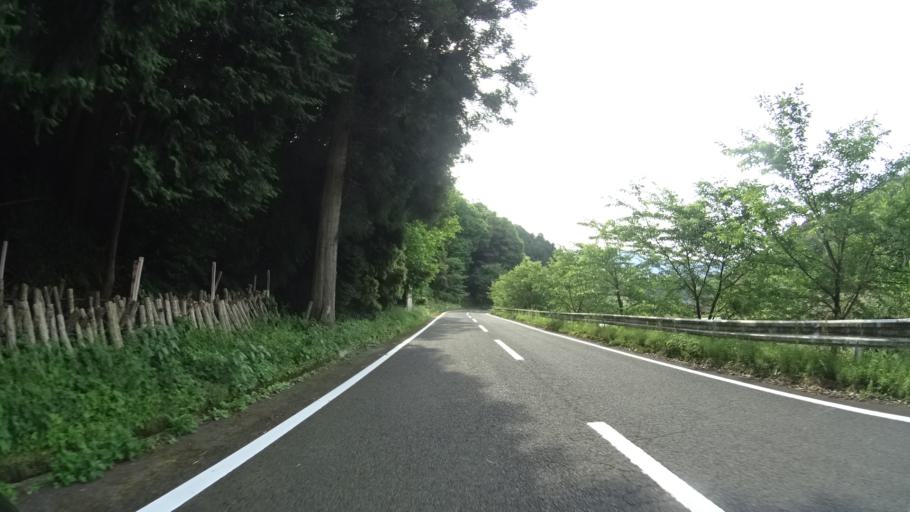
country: JP
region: Kyoto
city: Miyazu
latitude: 35.5023
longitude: 135.1333
